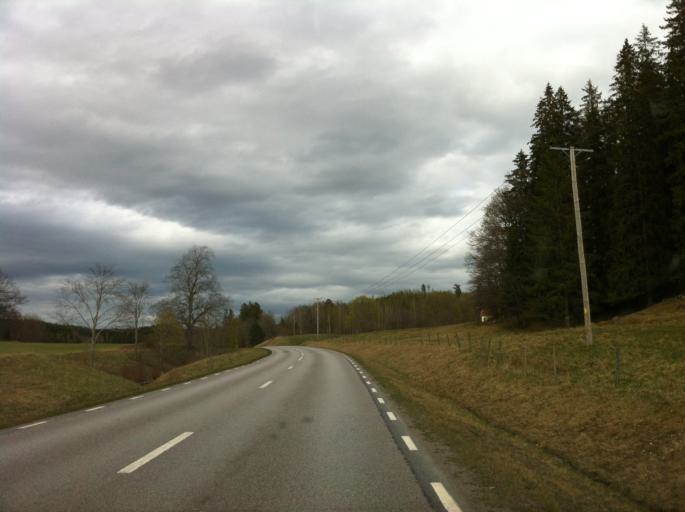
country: SE
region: OEstergoetland
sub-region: Kinda Kommun
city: Rimforsa
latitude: 58.0497
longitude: 15.8447
